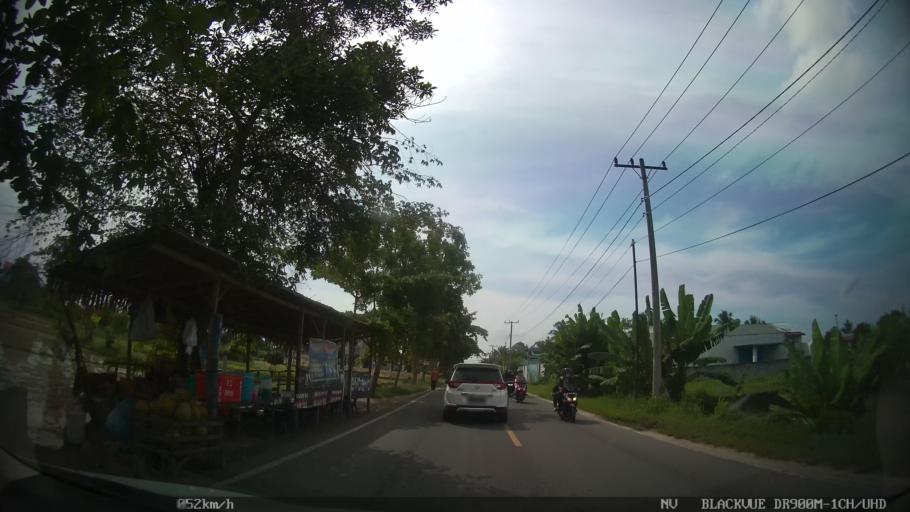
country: ID
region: North Sumatra
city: Percut
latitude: 3.6104
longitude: 98.8483
